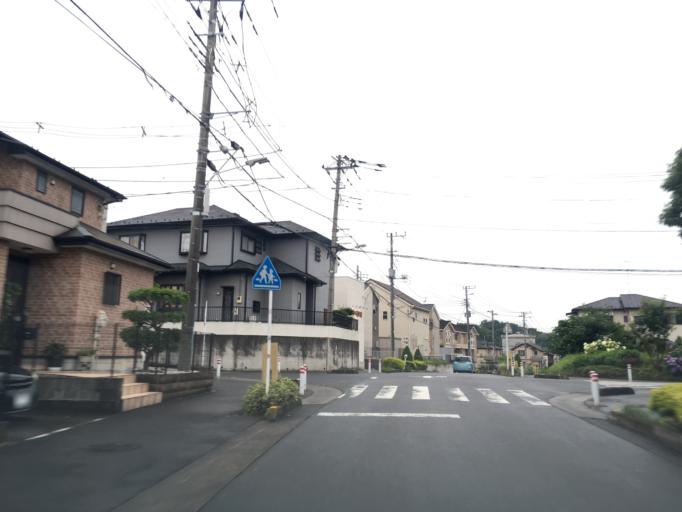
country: JP
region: Saitama
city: Tokorozawa
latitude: 35.7852
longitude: 139.4292
